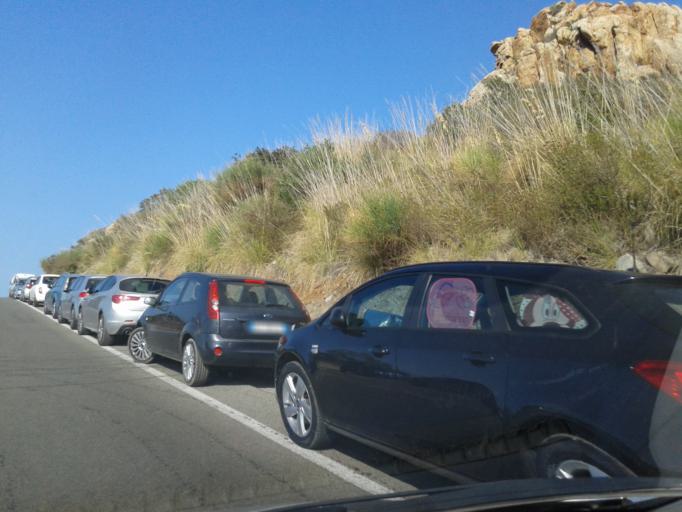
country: IT
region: Sicily
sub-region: Palermo
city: Finale
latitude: 38.0223
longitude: 14.1440
